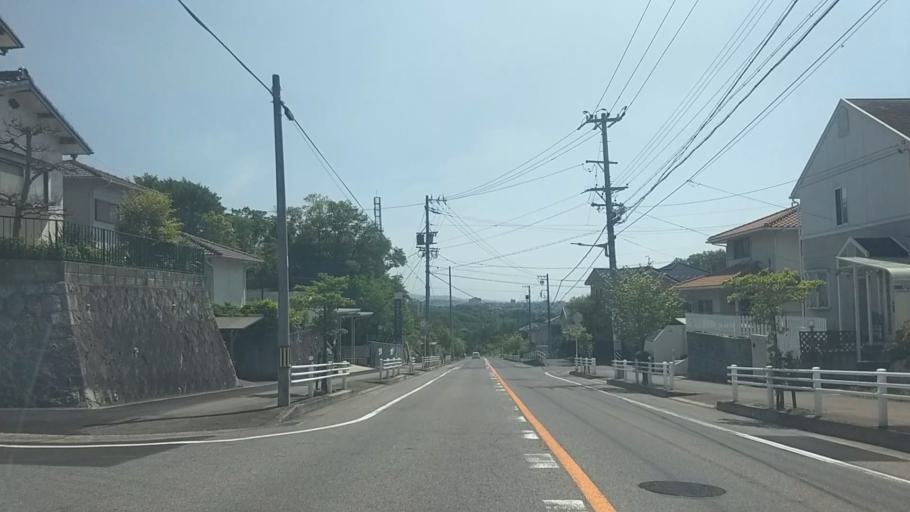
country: JP
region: Aichi
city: Okazaki
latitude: 34.9772
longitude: 137.1989
